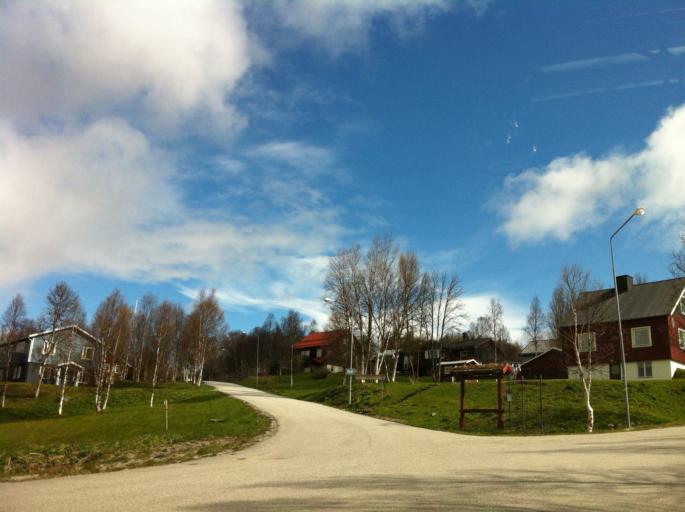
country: NO
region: Sor-Trondelag
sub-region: Tydal
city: Aas
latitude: 62.6256
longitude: 12.4510
